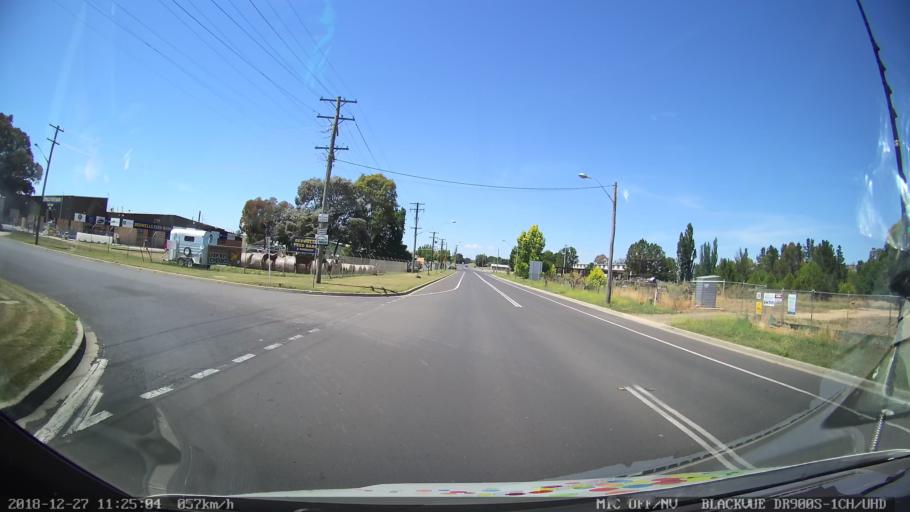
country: AU
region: New South Wales
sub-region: Bathurst Regional
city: Bathurst
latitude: -33.4386
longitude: 149.5785
